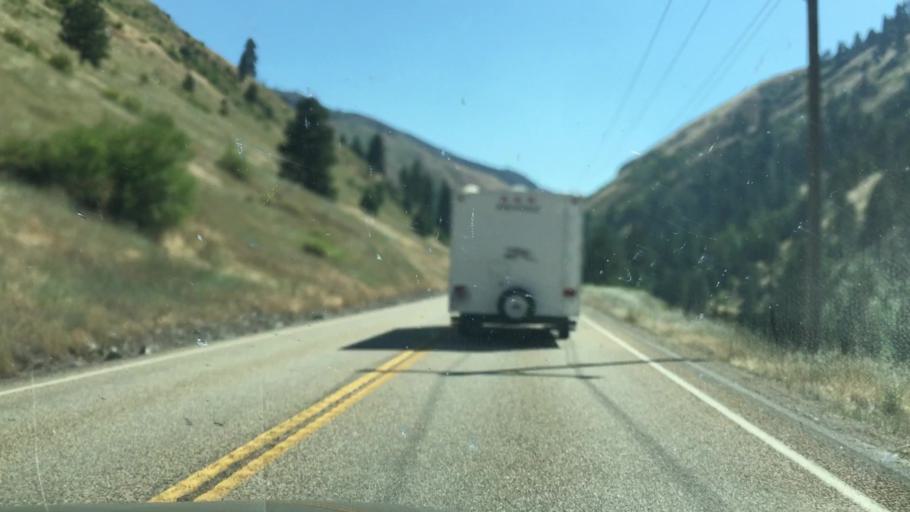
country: US
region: Idaho
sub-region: Boise County
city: Idaho City
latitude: 44.0420
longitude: -116.1313
